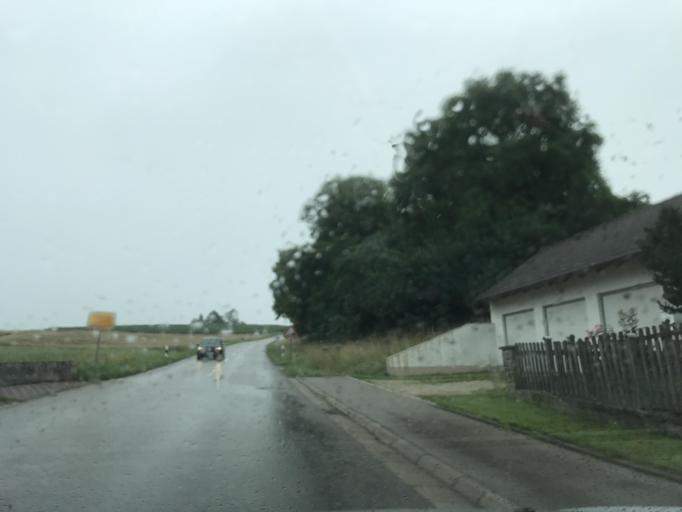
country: DE
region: Bavaria
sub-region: Upper Bavaria
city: Scheyern
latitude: 48.4624
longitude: 11.4491
